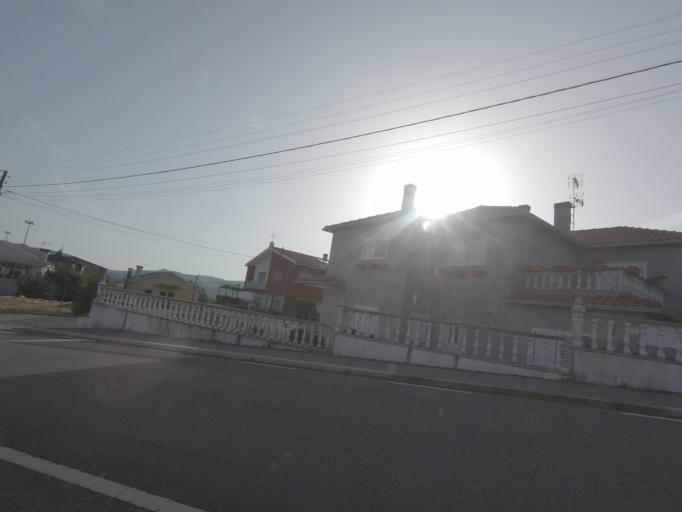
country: PT
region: Vila Real
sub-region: Sabrosa
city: Sabrosa
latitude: 41.2681
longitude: -7.4748
